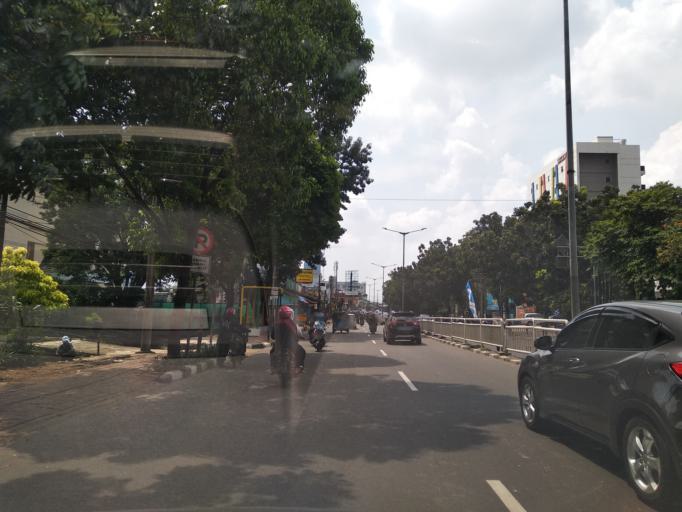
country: ID
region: Jakarta Raya
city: Jakarta
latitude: -6.2359
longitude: 106.8444
